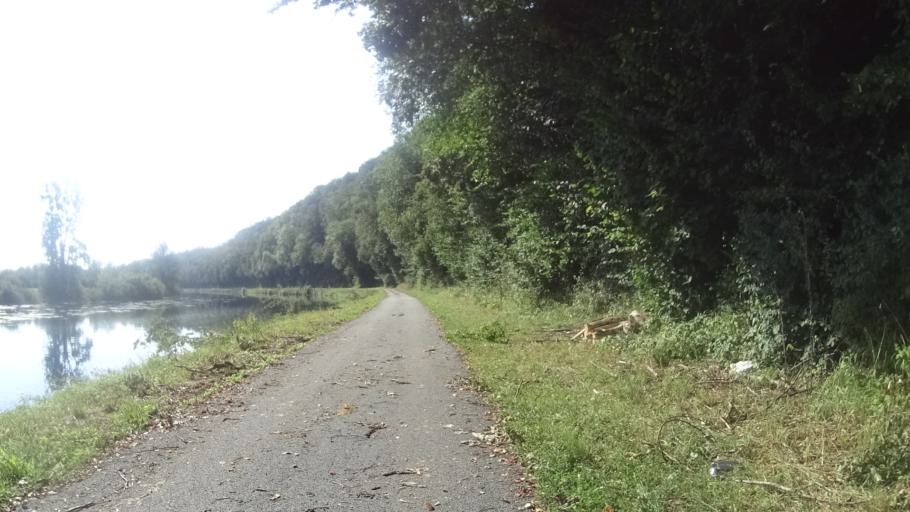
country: FR
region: Franche-Comte
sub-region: Departement du Doubs
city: Clerval
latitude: 47.4339
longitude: 6.5322
